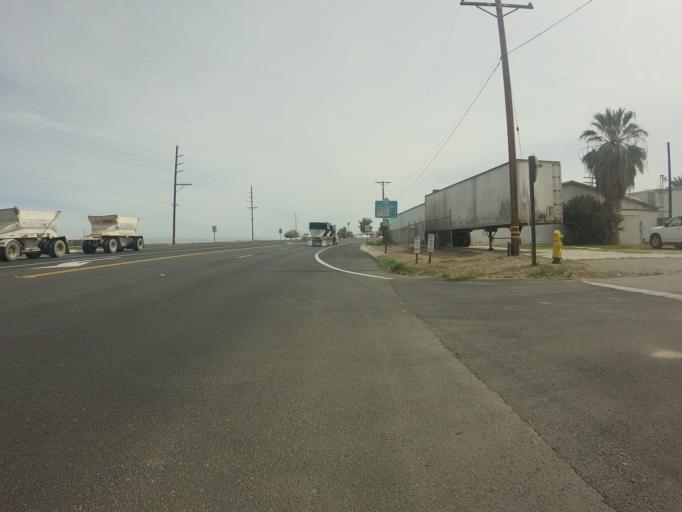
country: US
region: California
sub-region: Imperial County
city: Westmorland
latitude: 33.0373
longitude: -115.6173
